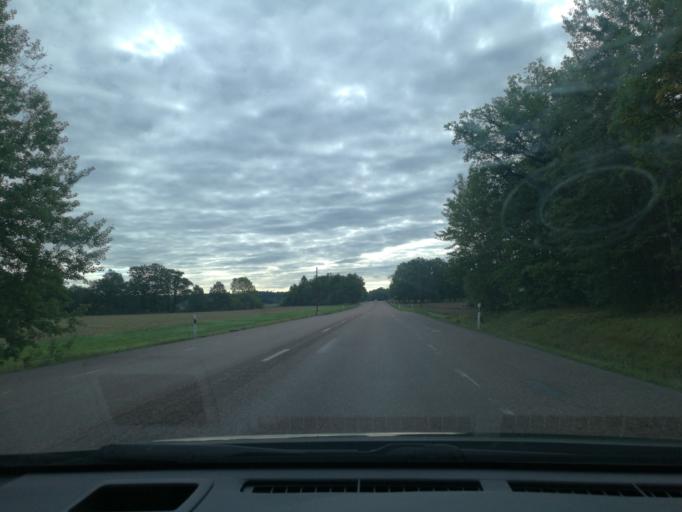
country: SE
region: Vaestmanland
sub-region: Kungsors Kommun
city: Kungsoer
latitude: 59.4370
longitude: 16.0568
